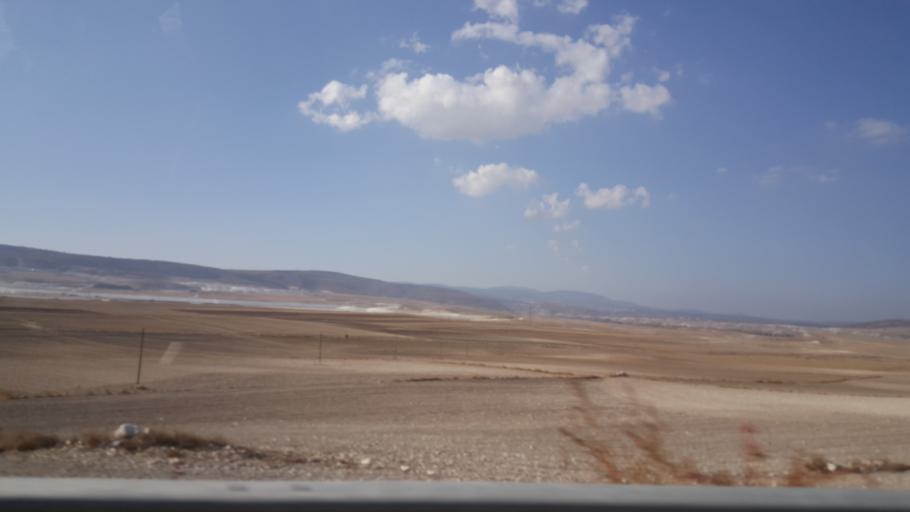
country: TR
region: Eskisehir
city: Kirka
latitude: 39.3072
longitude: 30.5338
